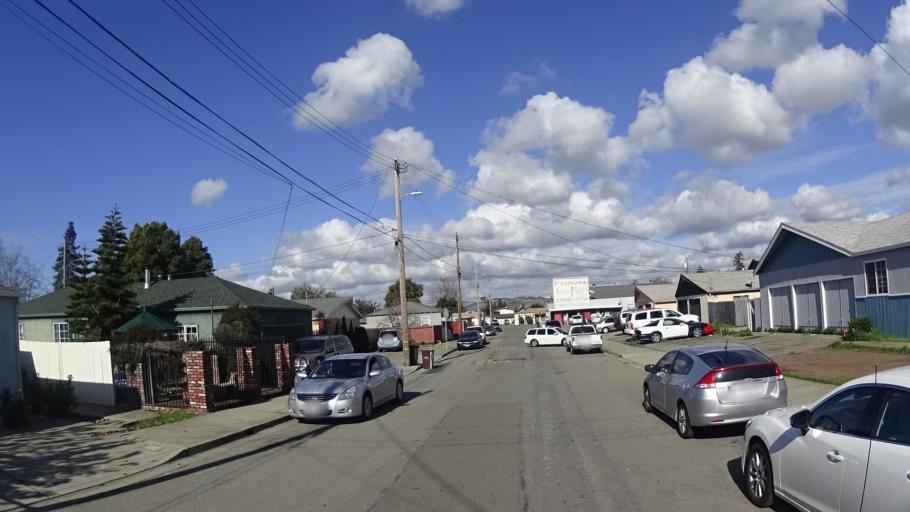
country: US
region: California
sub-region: Alameda County
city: Cherryland
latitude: 37.6596
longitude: -122.1094
